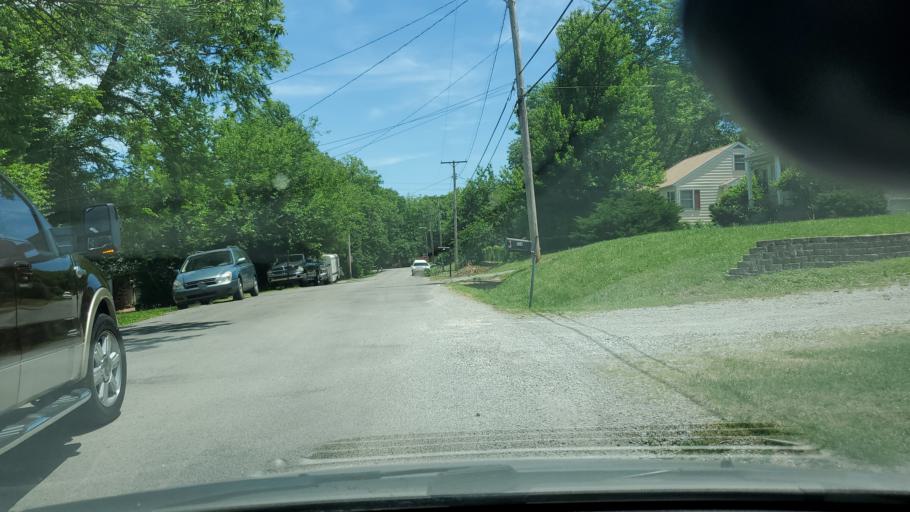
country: US
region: Tennessee
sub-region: Davidson County
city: Nashville
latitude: 36.2061
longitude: -86.7542
